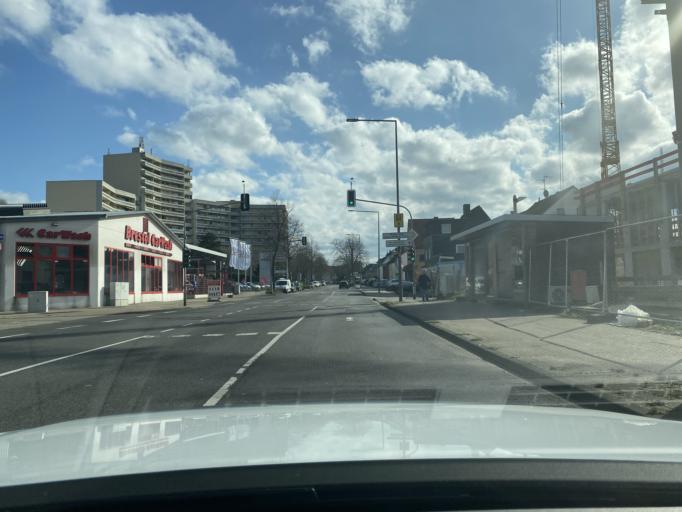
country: DE
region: North Rhine-Westphalia
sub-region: Regierungsbezirk Koln
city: Bergisch Gladbach
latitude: 50.9841
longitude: 7.1046
